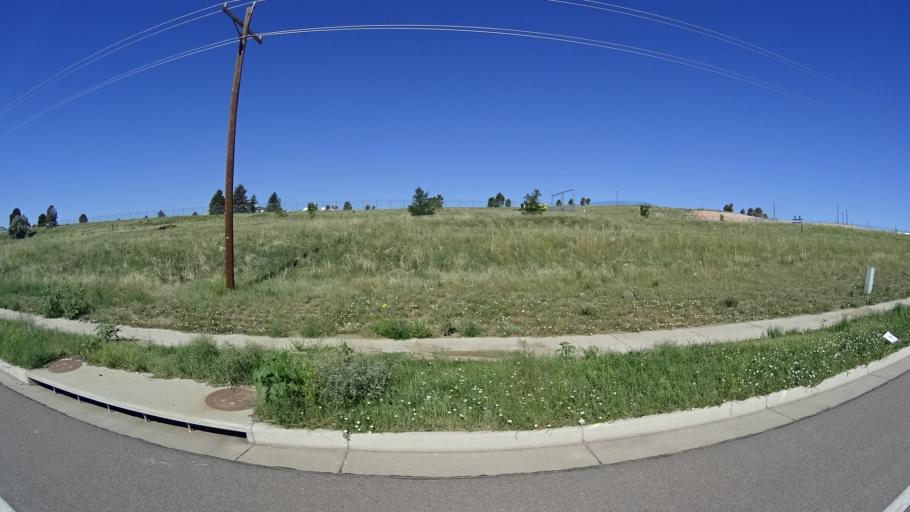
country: US
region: Colorado
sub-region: El Paso County
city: Cimarron Hills
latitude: 38.8822
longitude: -104.6829
